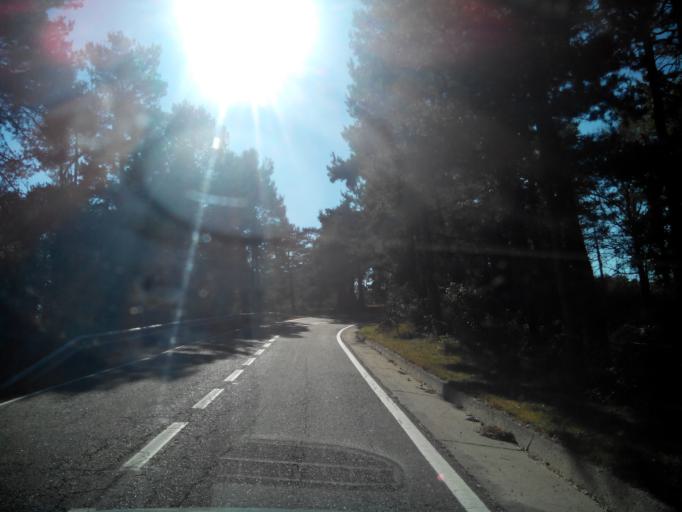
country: ES
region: Catalonia
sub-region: Provincia de Barcelona
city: Capolat
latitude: 42.0910
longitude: 1.7815
